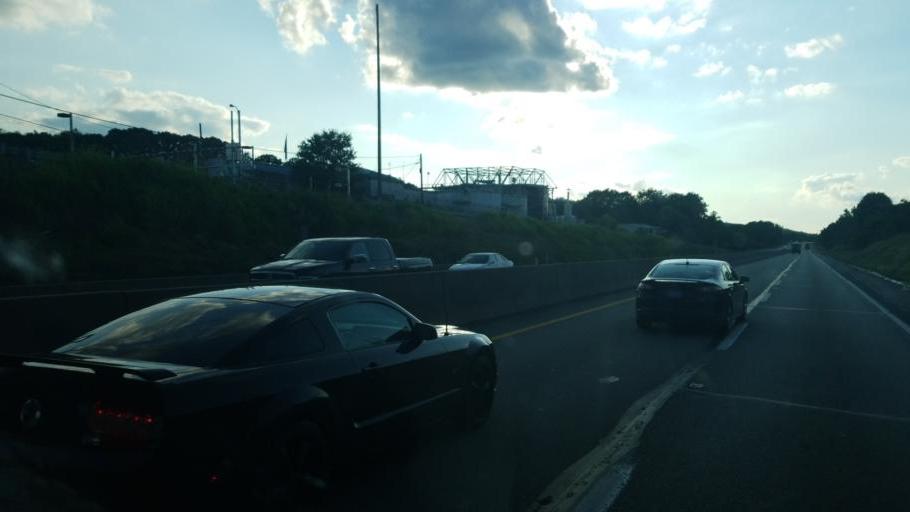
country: US
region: Pennsylvania
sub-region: Butler County
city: Fernway
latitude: 40.7196
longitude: -80.1436
